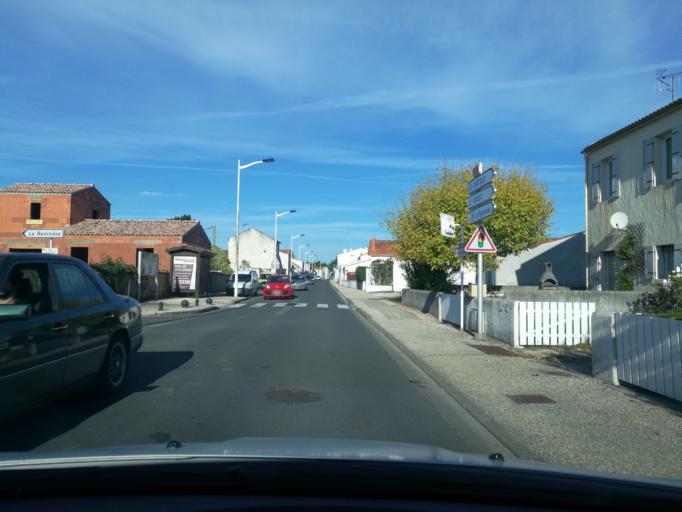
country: FR
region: Poitou-Charentes
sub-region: Departement de la Charente-Maritime
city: Saint-Trojan-les-Bains
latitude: 45.8907
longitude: -1.2203
